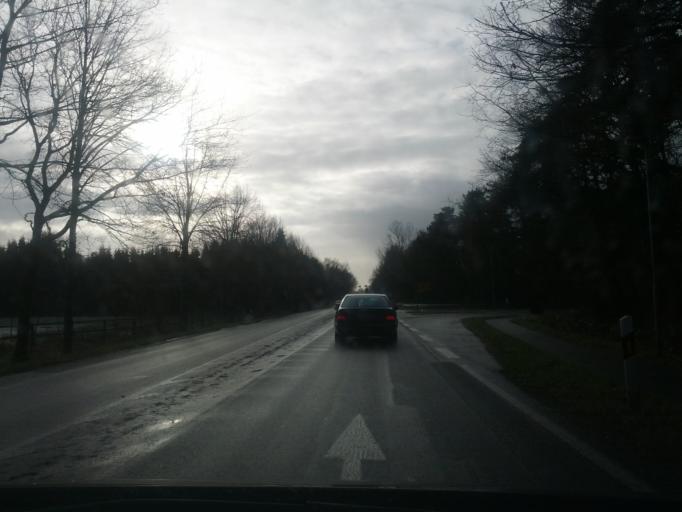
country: DE
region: Lower Saxony
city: Lengenbostel
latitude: 53.2973
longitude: 9.5089
